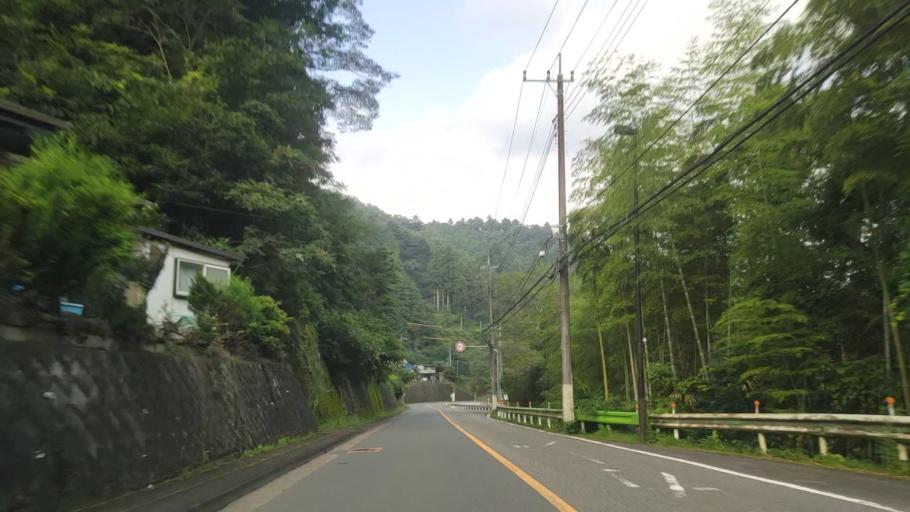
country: JP
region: Tokyo
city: Ome
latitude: 35.8329
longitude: 139.2233
